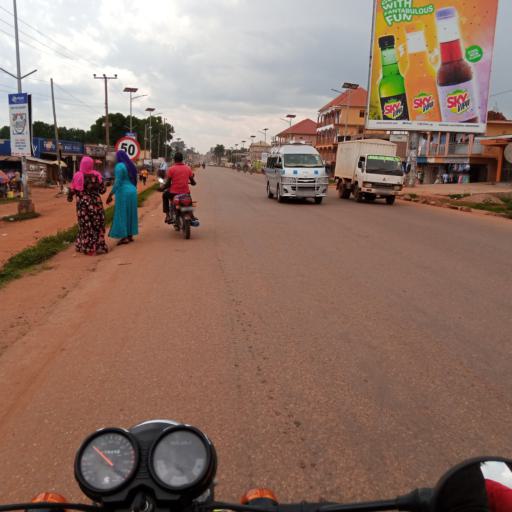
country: UG
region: Eastern Region
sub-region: Mbale District
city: Mbale
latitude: 1.0873
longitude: 34.1780
